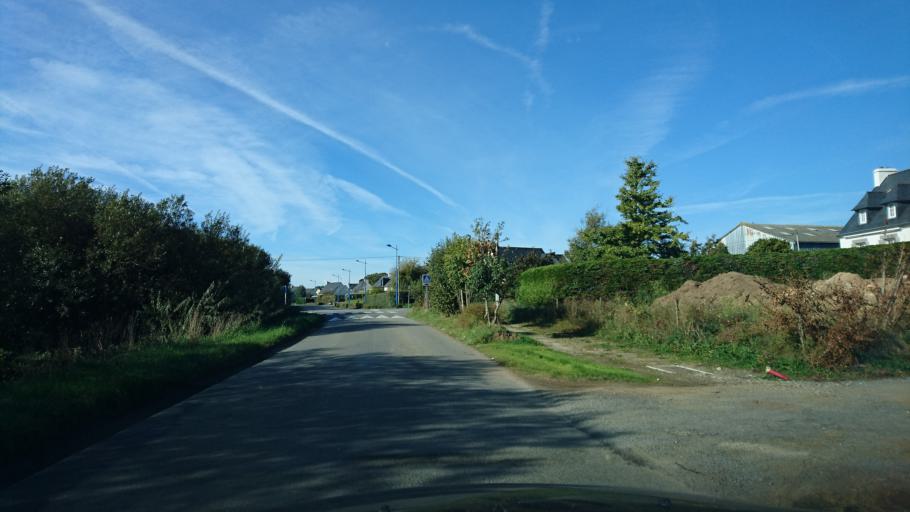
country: FR
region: Brittany
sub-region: Departement du Finistere
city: Plouarzel
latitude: 48.4325
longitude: -4.7284
